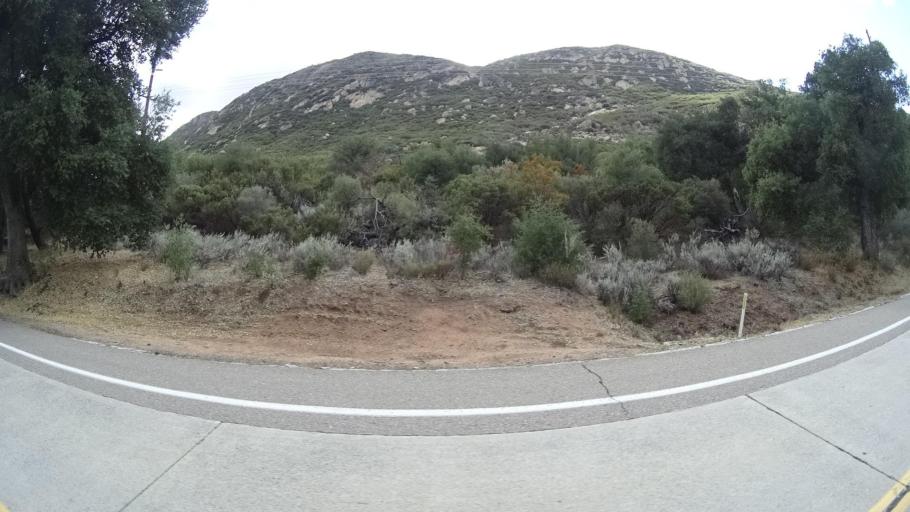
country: US
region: California
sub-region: San Diego County
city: Pine Valley
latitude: 32.8009
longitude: -116.5015
